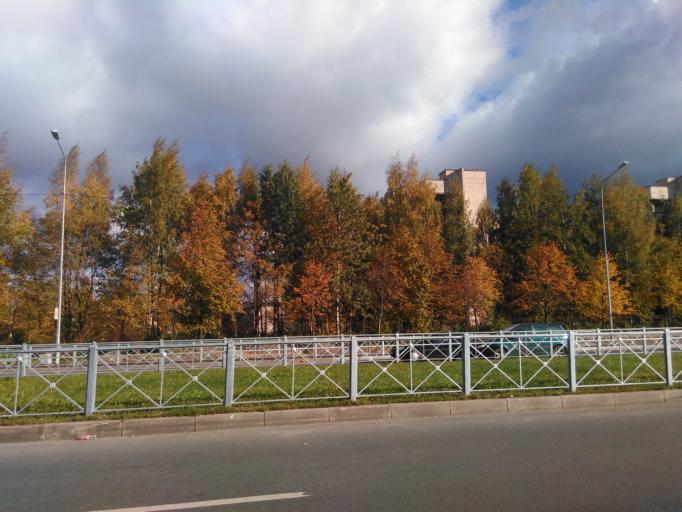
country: RU
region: St.-Petersburg
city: Krasnogvargeisky
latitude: 59.9279
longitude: 30.4861
